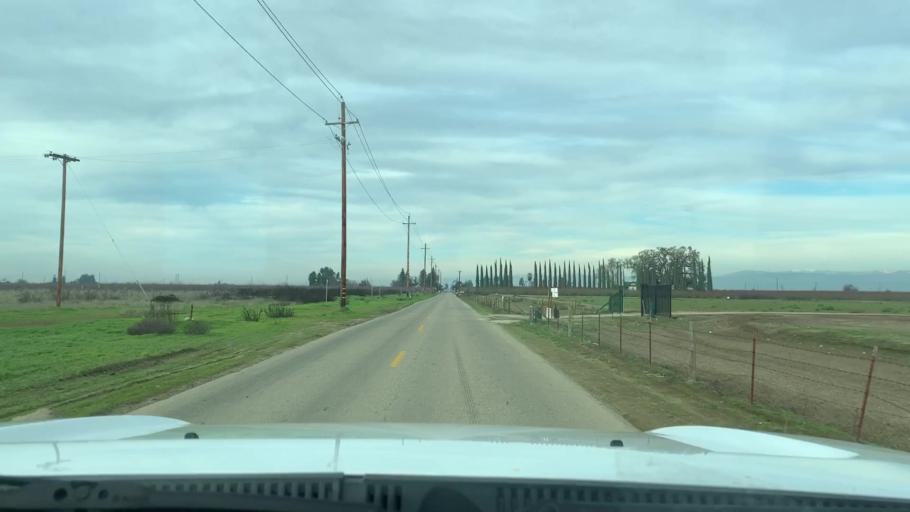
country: US
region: California
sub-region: Fresno County
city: Selma
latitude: 36.5976
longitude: -119.5748
